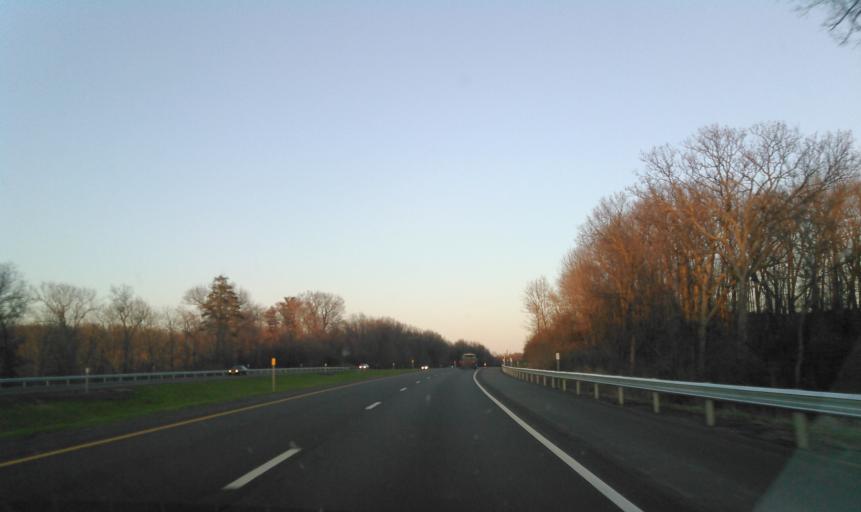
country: US
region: New York
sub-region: Ontario County
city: Geneva
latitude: 42.9597
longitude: -76.9466
